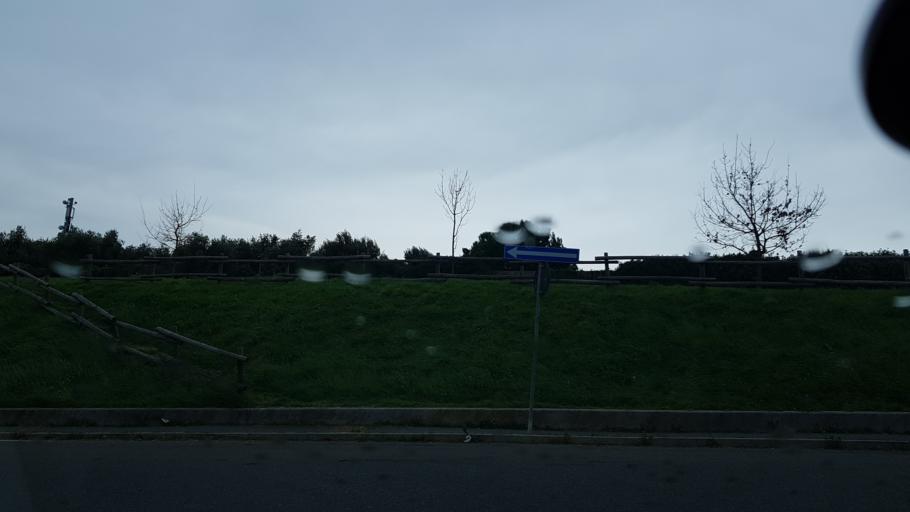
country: IT
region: Liguria
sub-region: Provincia di Savona
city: Savona
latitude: 44.3006
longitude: 8.4584
